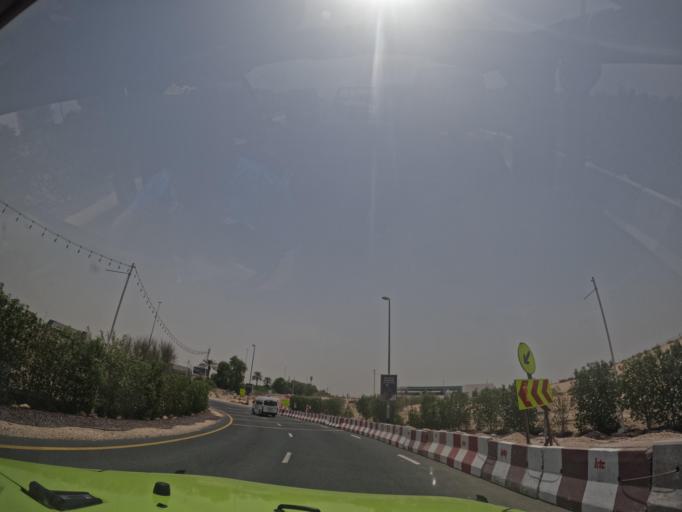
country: AE
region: Dubai
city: Dubai
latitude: 25.0749
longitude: 55.3034
